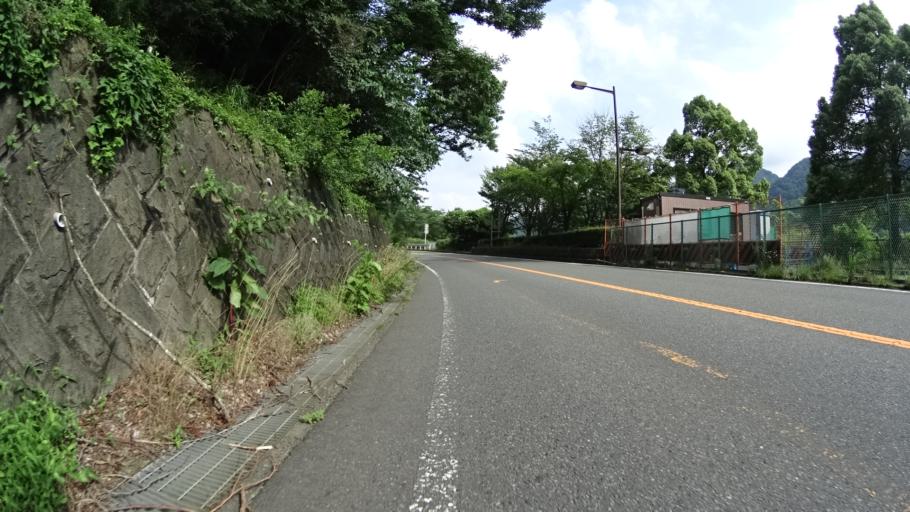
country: JP
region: Kanagawa
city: Atsugi
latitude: 35.5166
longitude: 139.2420
